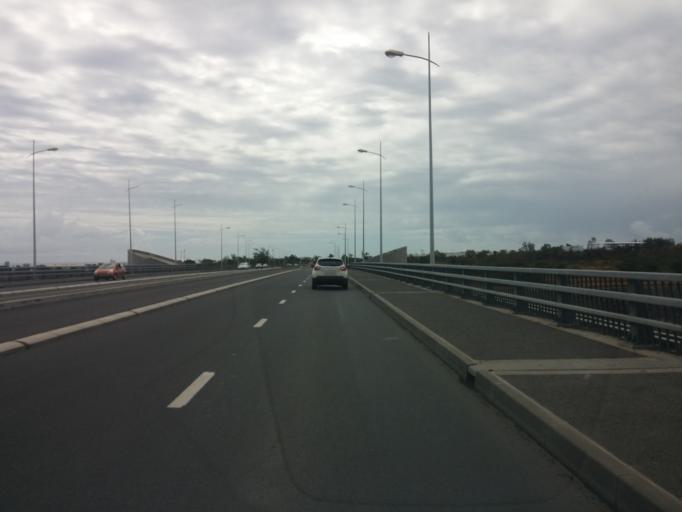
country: RE
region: Reunion
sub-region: Reunion
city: Le Port
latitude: -20.9571
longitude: 55.2940
